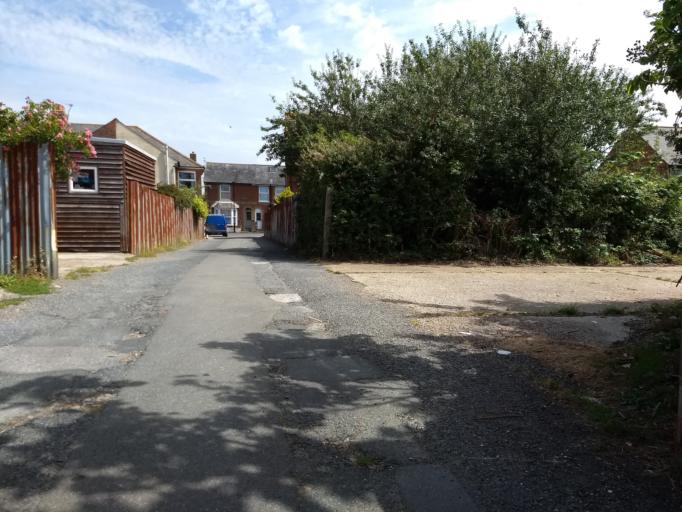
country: GB
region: England
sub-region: Isle of Wight
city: Newport
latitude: 50.7060
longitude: -1.3018
